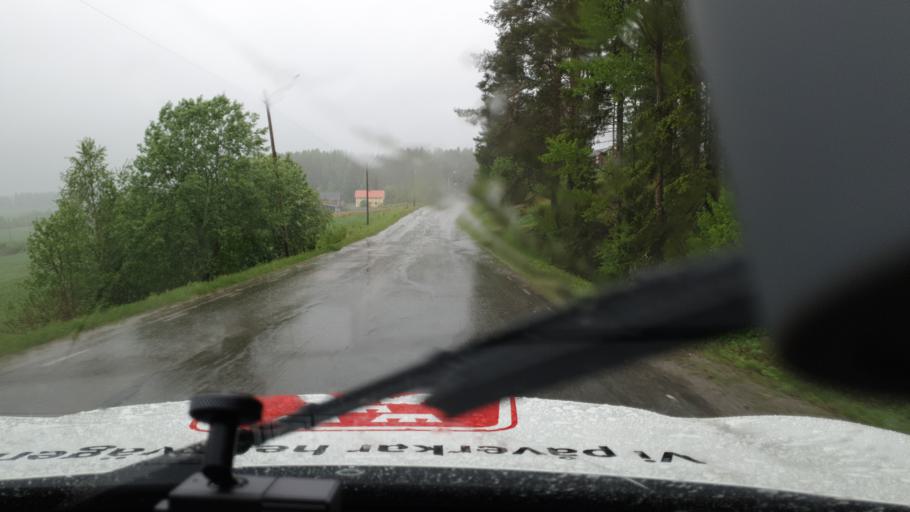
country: SE
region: Vaesterbotten
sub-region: Umea Kommun
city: Roback
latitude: 64.0316
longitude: 20.0841
